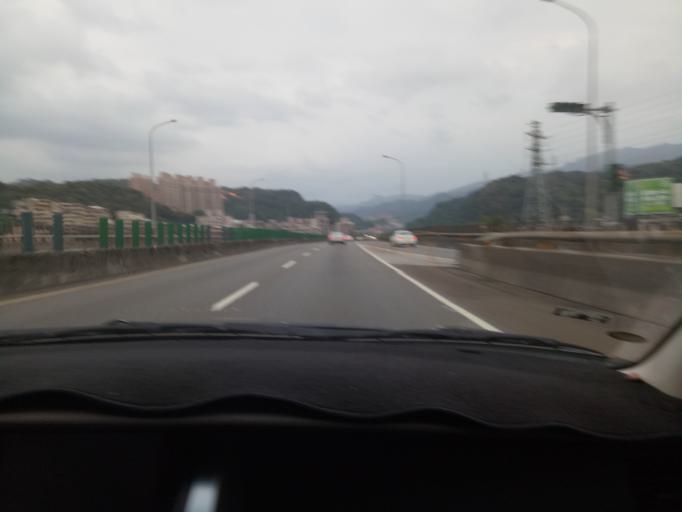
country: TW
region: Taiwan
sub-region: Keelung
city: Keelung
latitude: 25.1047
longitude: 121.7349
